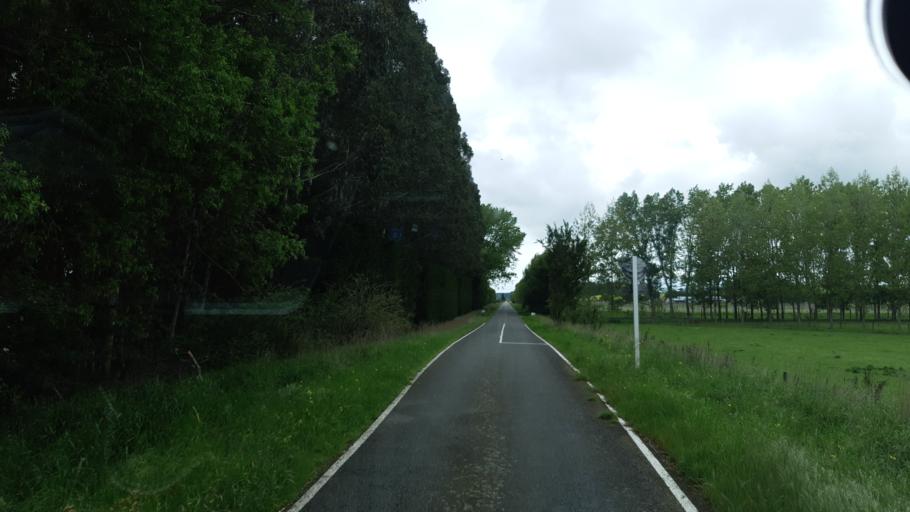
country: NZ
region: Canterbury
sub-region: Timaru District
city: Pleasant Point
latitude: -44.3031
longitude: 171.1645
